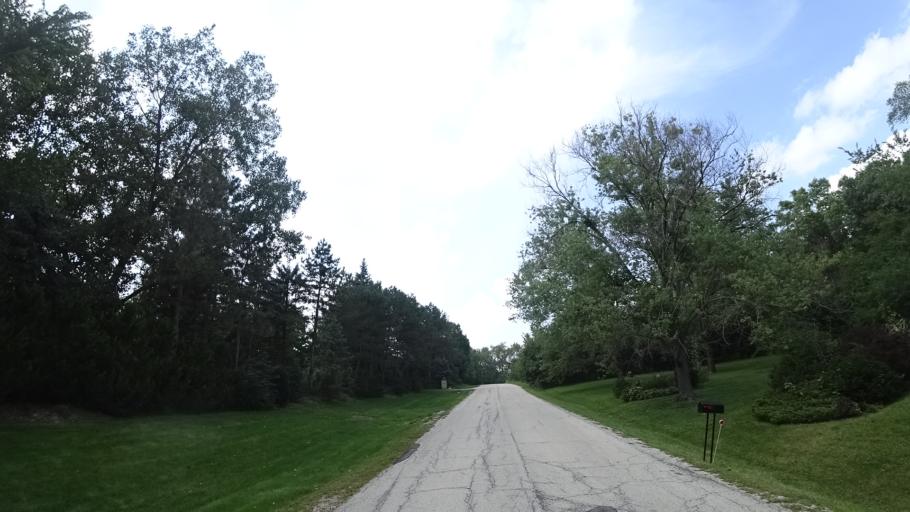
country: US
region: Illinois
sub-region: Will County
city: Goodings Grove
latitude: 41.6608
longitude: -87.8984
